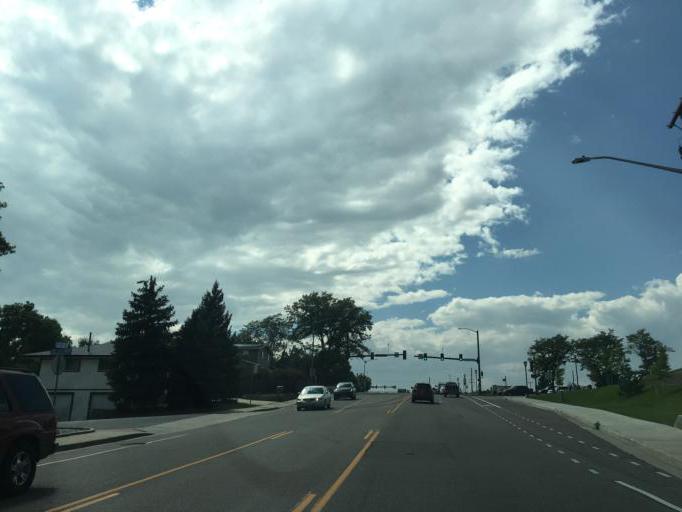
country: US
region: Colorado
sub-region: Jefferson County
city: Applewood
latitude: 39.7619
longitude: -105.1391
